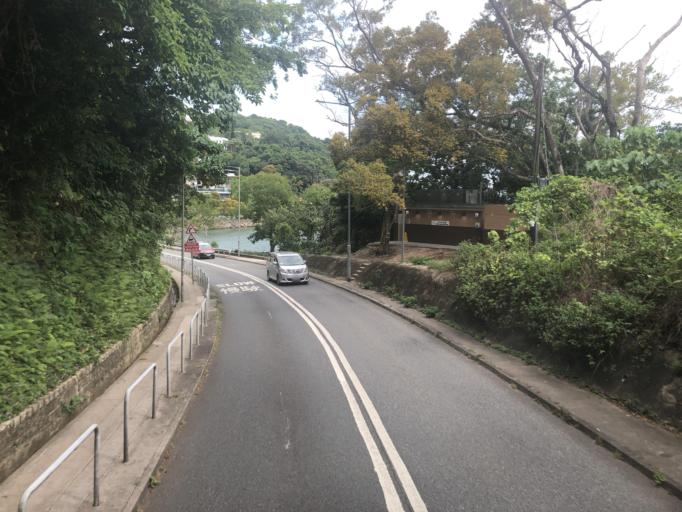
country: HK
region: Sai Kung
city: Sai Kung
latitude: 22.3949
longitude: 114.2877
